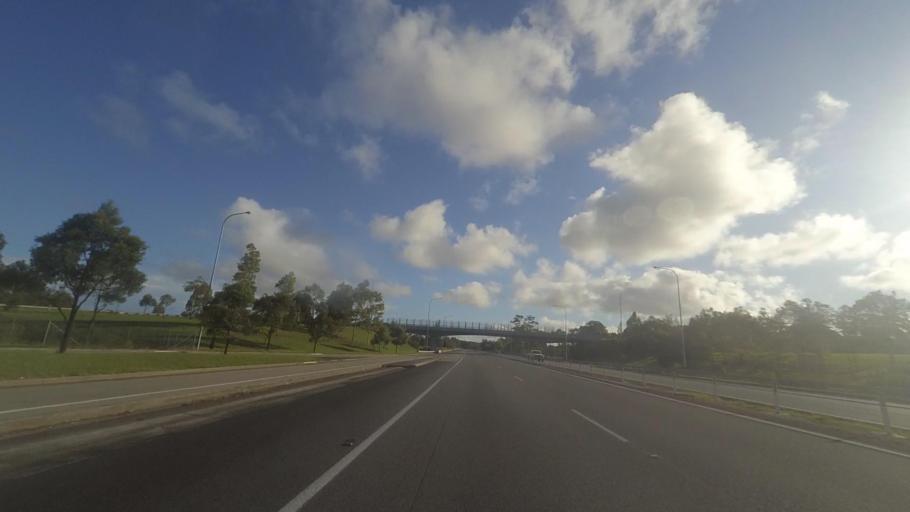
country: AU
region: New South Wales
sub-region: Great Lakes
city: Nabiac
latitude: -32.1002
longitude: 152.3756
